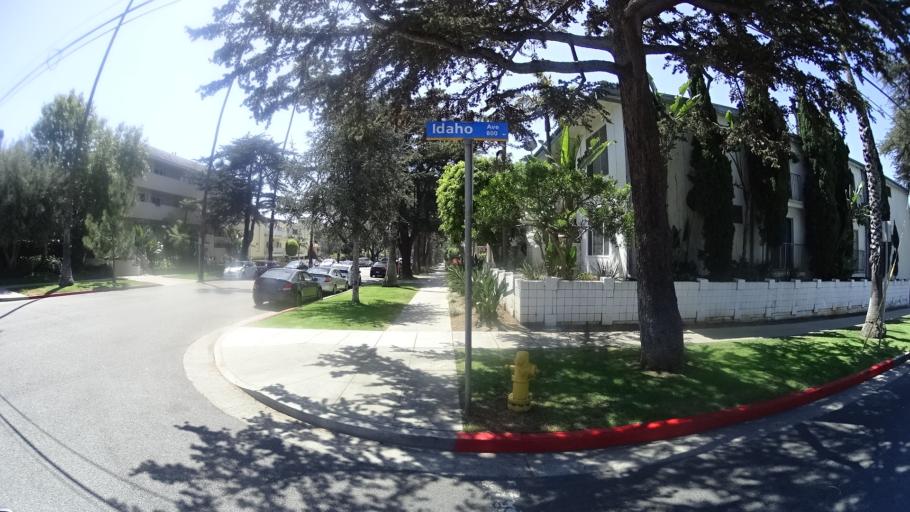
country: US
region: California
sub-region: Los Angeles County
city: Santa Monica
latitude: 34.0269
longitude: -118.4984
